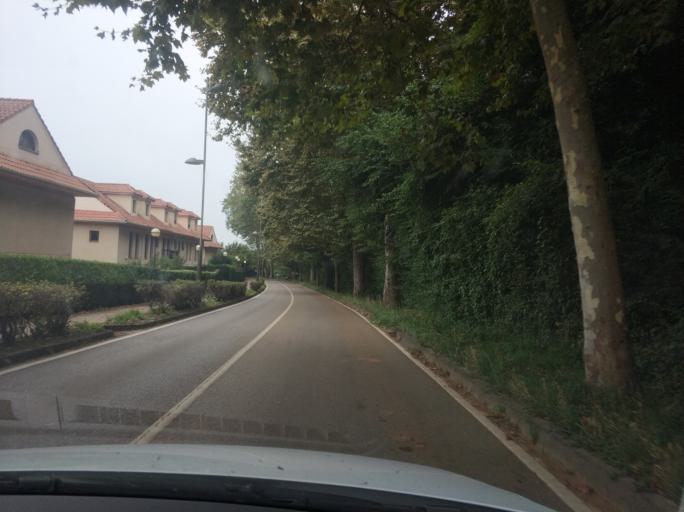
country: ES
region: Cantabria
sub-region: Provincia de Cantabria
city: Comillas
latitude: 43.3836
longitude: -4.3016
